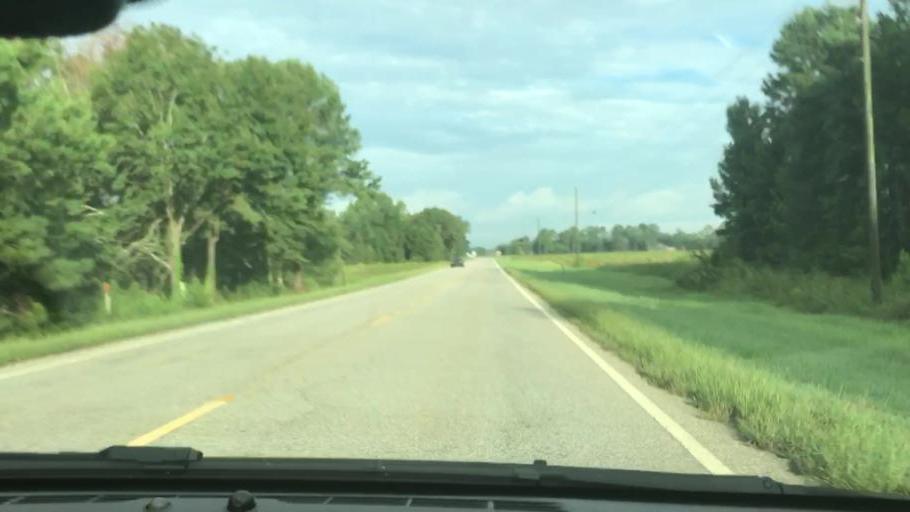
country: US
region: Georgia
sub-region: Quitman County
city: Georgetown
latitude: 31.7576
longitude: -85.0669
